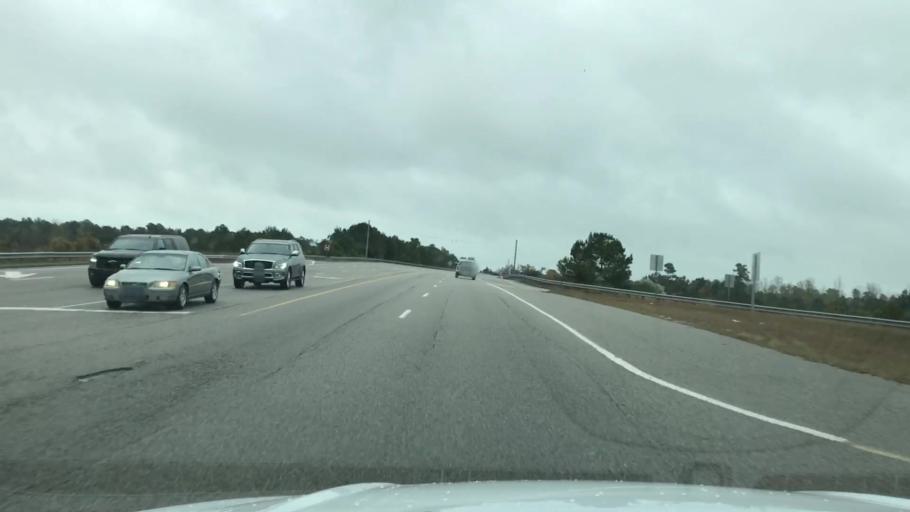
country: US
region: South Carolina
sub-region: Horry County
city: Myrtle Beach
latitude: 33.7562
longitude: -78.8549
